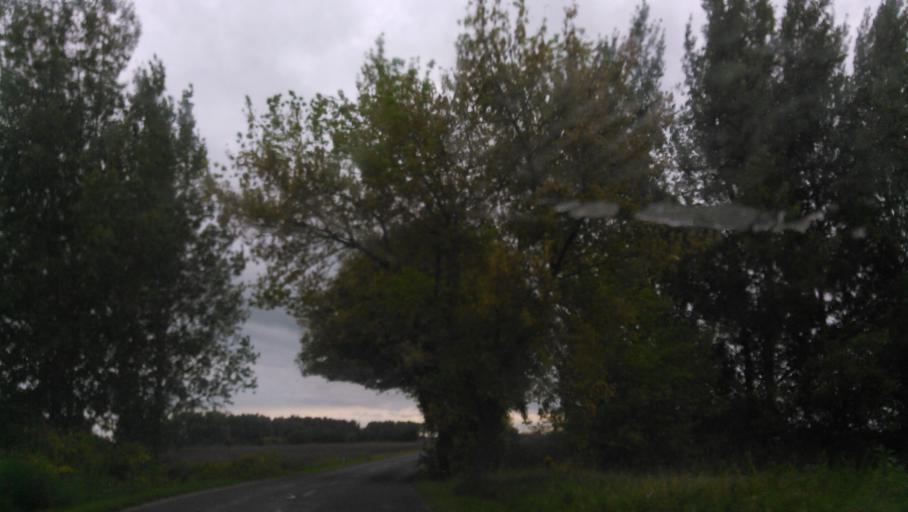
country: SK
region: Trnavsky
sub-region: Okres Dunajska Streda
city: Velky Meder
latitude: 47.9166
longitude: 17.7485
